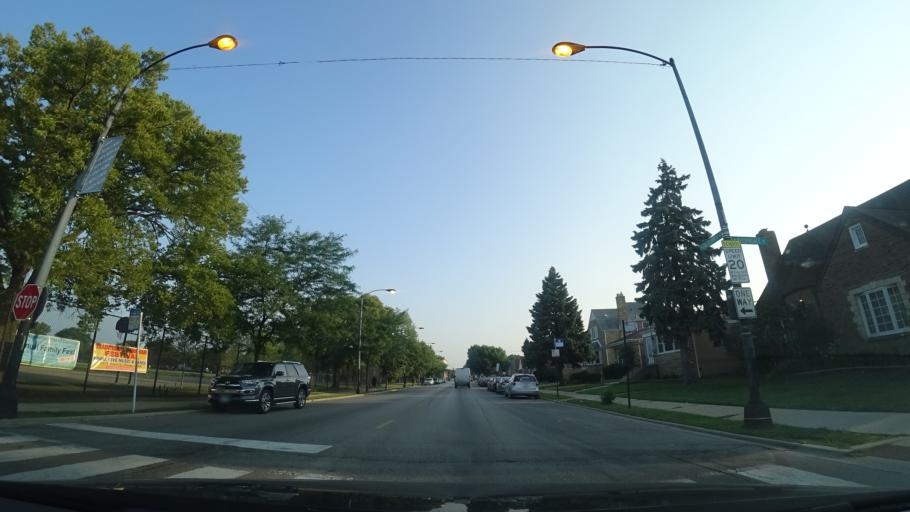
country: US
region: Illinois
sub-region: Cook County
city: Lincolnwood
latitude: 41.9886
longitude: -87.6993
